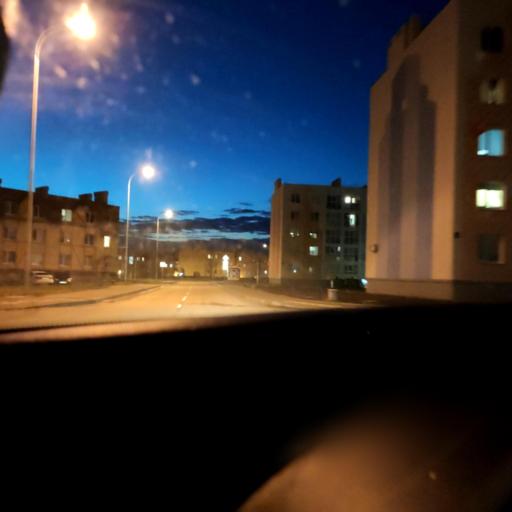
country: RU
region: Samara
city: Petra-Dubrava
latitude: 53.2958
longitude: 50.3193
